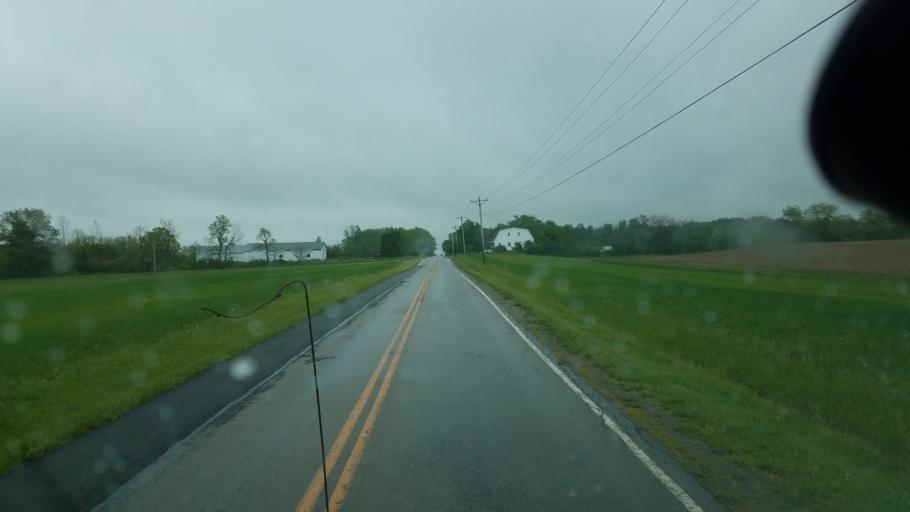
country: US
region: Ohio
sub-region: Highland County
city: Greenfield
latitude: 39.3417
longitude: -83.4446
